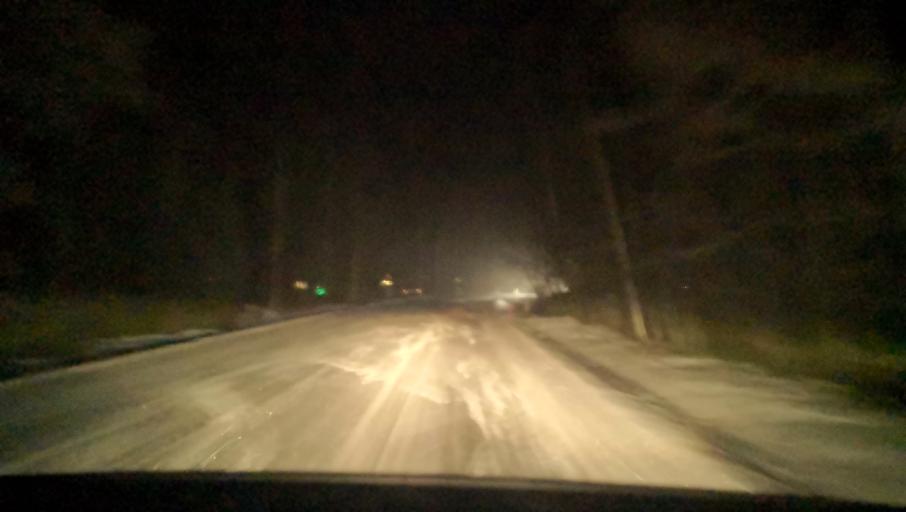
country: SE
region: Uppsala
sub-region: Heby Kommun
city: Tarnsjo
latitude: 60.1409
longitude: 16.9081
